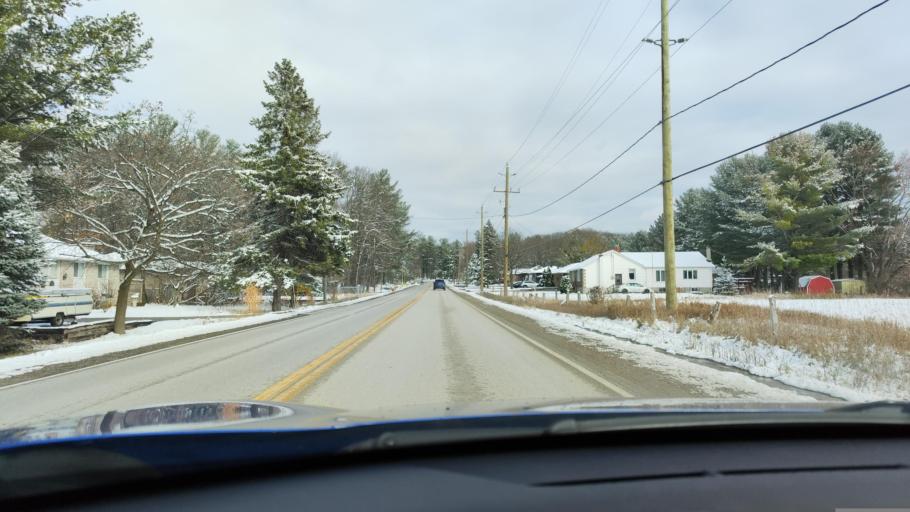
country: CA
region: Ontario
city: Barrie
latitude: 44.3811
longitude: -79.7639
